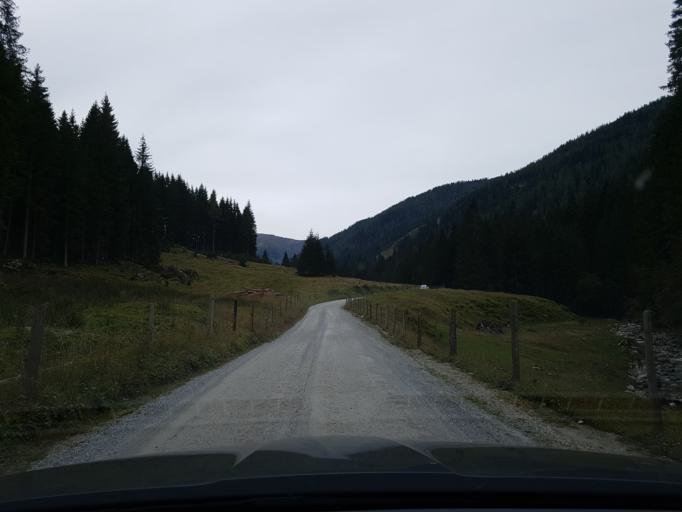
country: AT
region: Salzburg
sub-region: Politischer Bezirk Sankt Johann im Pongau
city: Forstau
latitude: 47.3314
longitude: 13.5776
